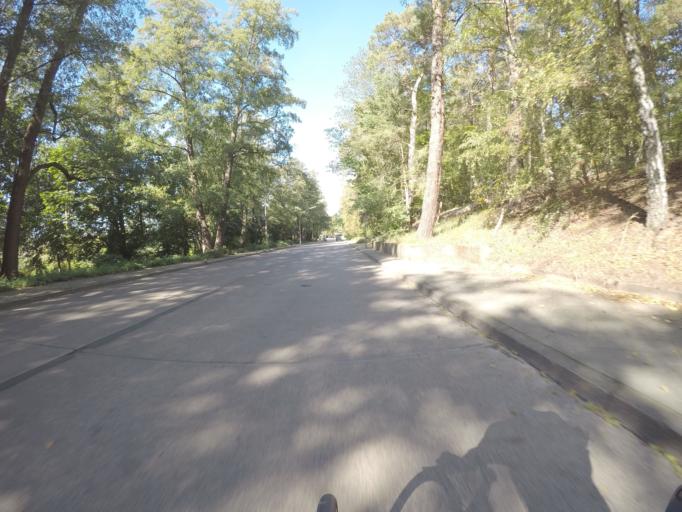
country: DE
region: Berlin
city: Konradshohe
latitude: 52.5932
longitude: 13.2227
